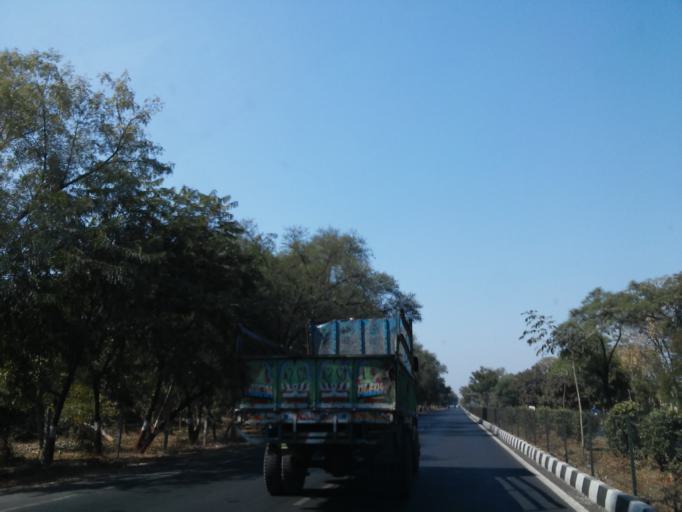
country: IN
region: Gujarat
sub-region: Gandhinagar
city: Ghandinagar
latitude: 23.2373
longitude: 72.7130
